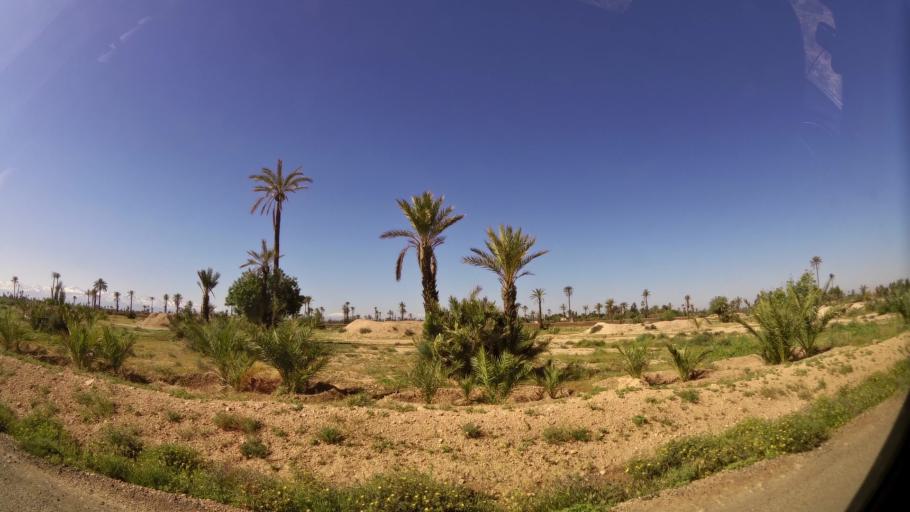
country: MA
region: Marrakech-Tensift-Al Haouz
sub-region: Marrakech
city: Marrakesh
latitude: 31.6679
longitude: -7.9537
